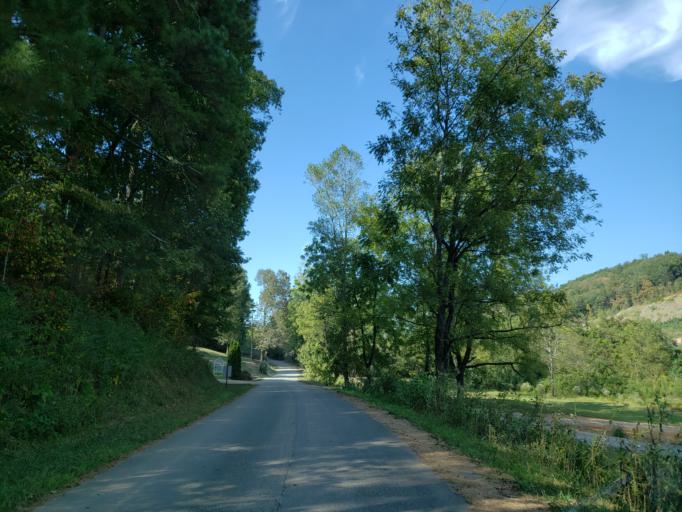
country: US
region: Georgia
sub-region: Gilmer County
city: Ellijay
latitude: 34.5901
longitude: -84.5110
